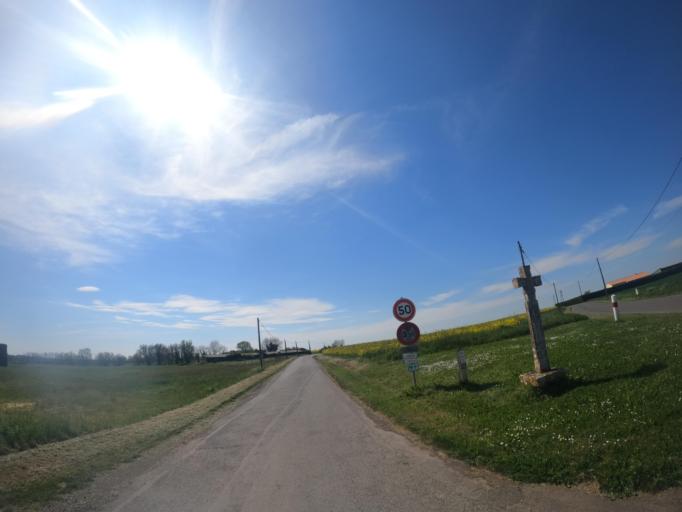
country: FR
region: Poitou-Charentes
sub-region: Departement des Deux-Sevres
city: Airvault
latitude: 46.8858
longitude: -0.1485
